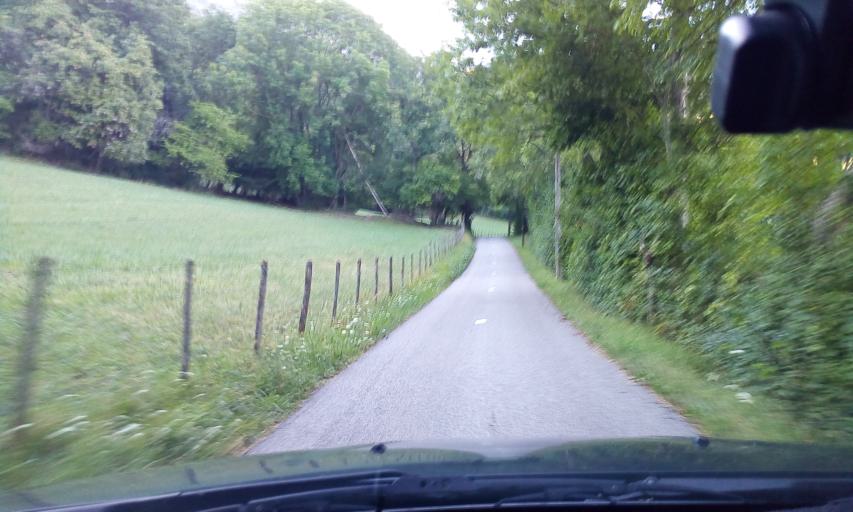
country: FR
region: Rhone-Alpes
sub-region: Departement de la Savoie
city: Saint-Baldoph
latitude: 45.5188
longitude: 5.9240
